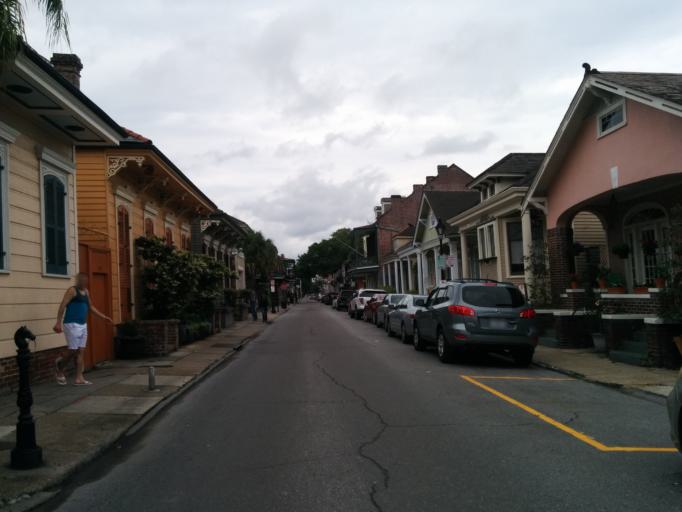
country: US
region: Louisiana
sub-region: Orleans Parish
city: New Orleans
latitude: 29.9623
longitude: -90.0599
